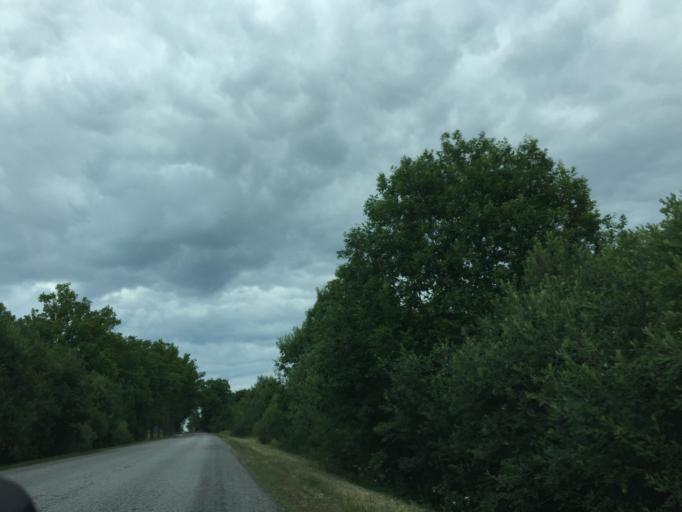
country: LV
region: Skriveri
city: Skriveri
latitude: 56.8315
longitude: 25.1291
